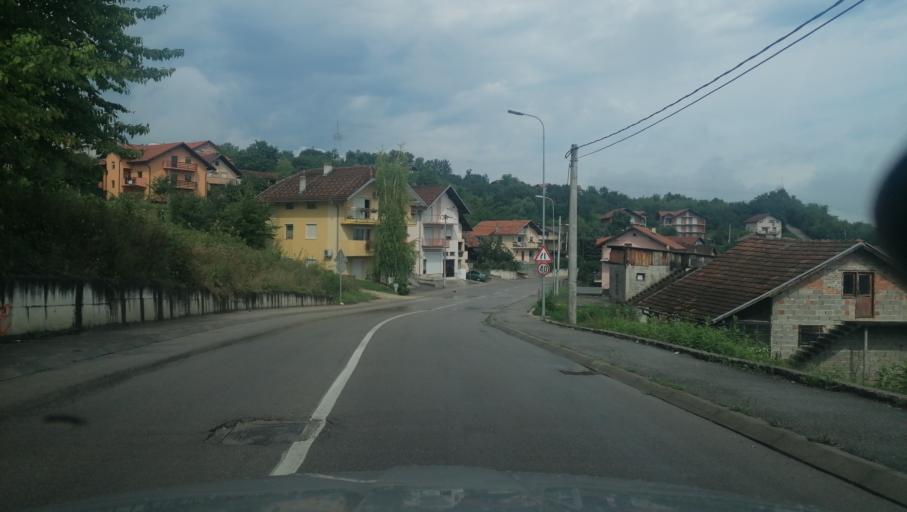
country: BA
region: Republika Srpska
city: Banja Luka
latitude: 44.7878
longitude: 17.1733
